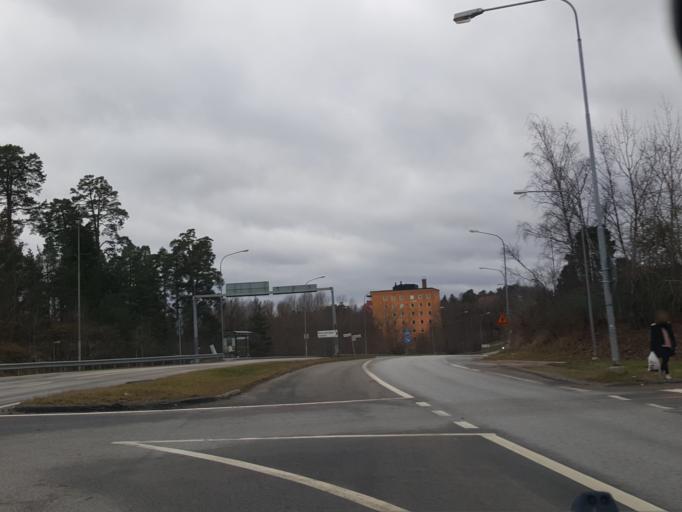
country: SE
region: Stockholm
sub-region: Lidingo
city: Brevik
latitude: 59.3145
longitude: 18.2135
